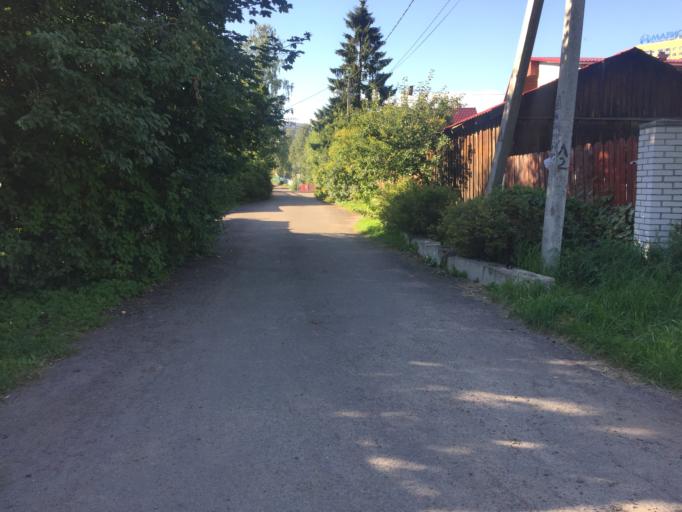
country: RU
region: Leningrad
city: Murino
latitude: 60.0464
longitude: 30.4447
